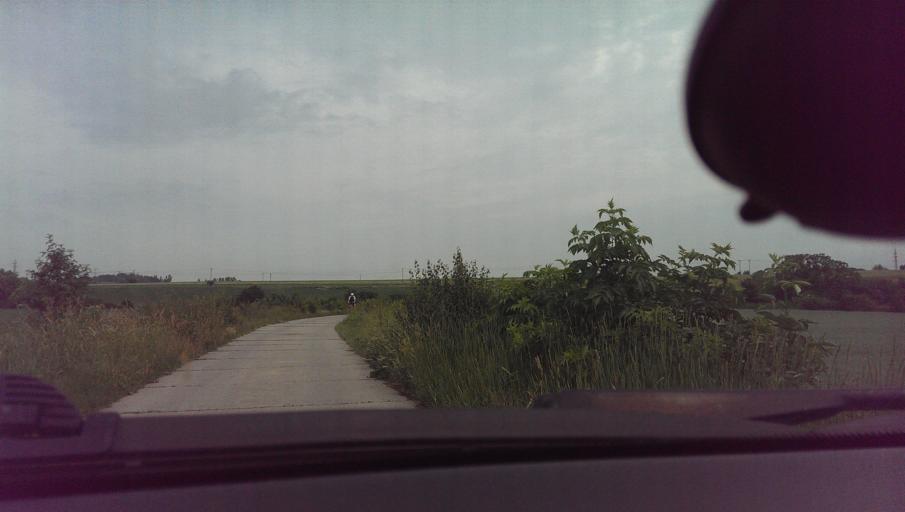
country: CZ
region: Zlin
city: Tecovice
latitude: 49.2124
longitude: 17.5758
